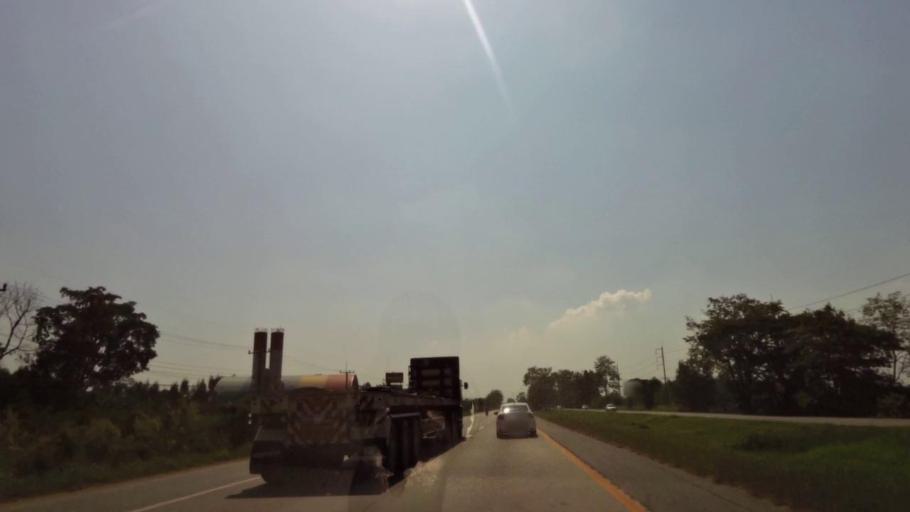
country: TH
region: Phichit
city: Wachira Barami
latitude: 16.5995
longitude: 100.1476
